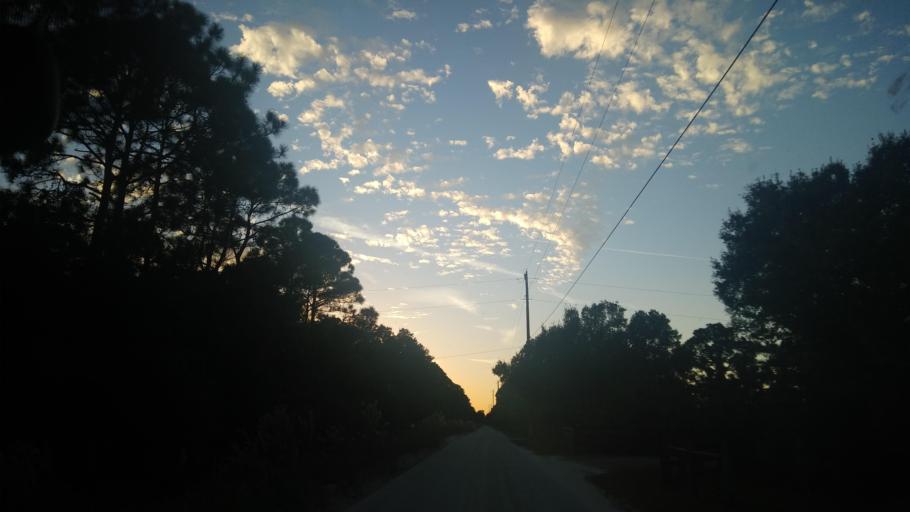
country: US
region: Florida
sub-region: Indian River County
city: Fellsmere
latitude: 27.7467
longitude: -80.6033
